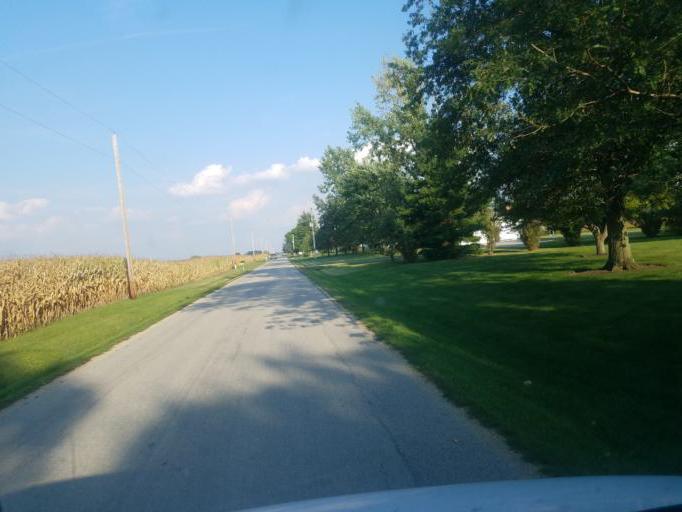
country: US
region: Ohio
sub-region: Wyandot County
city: Upper Sandusky
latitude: 40.9352
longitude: -83.1742
